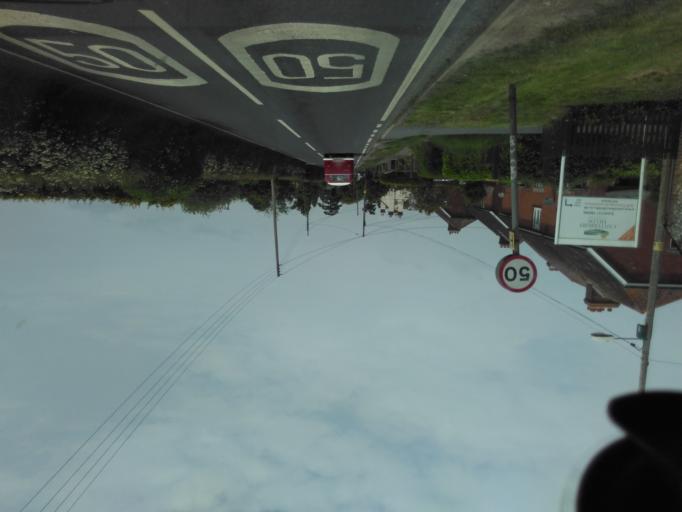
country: GB
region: England
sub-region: Kent
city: Chartham
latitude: 51.2154
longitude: 1.0601
